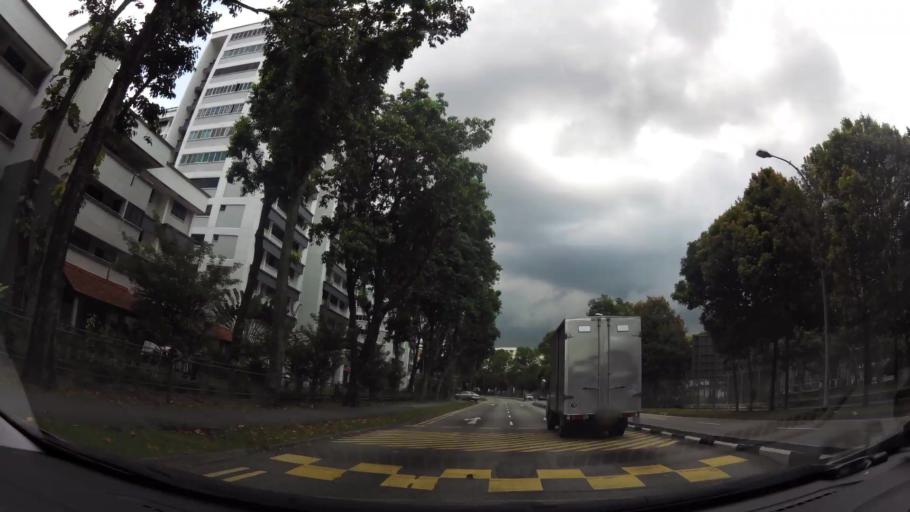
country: MY
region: Johor
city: Kampung Pasir Gudang Baru
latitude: 1.4218
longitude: 103.8315
